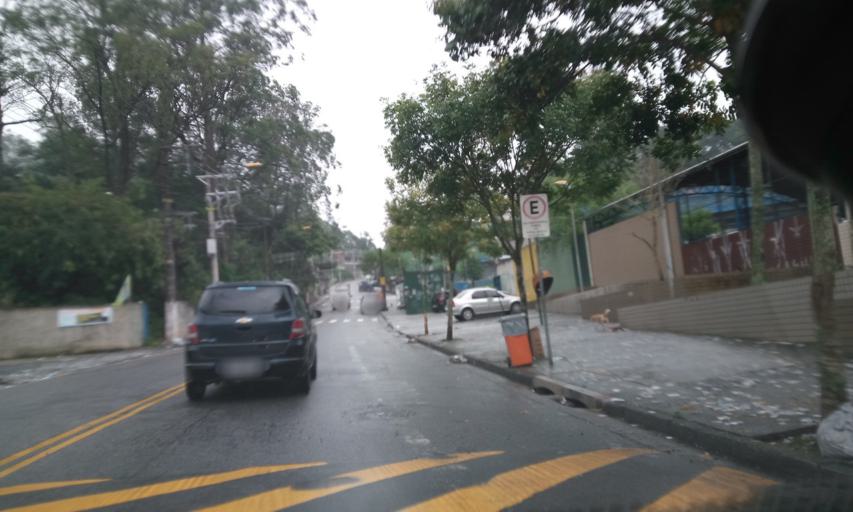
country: BR
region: Sao Paulo
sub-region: Maua
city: Maua
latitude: -23.7399
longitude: -46.4962
